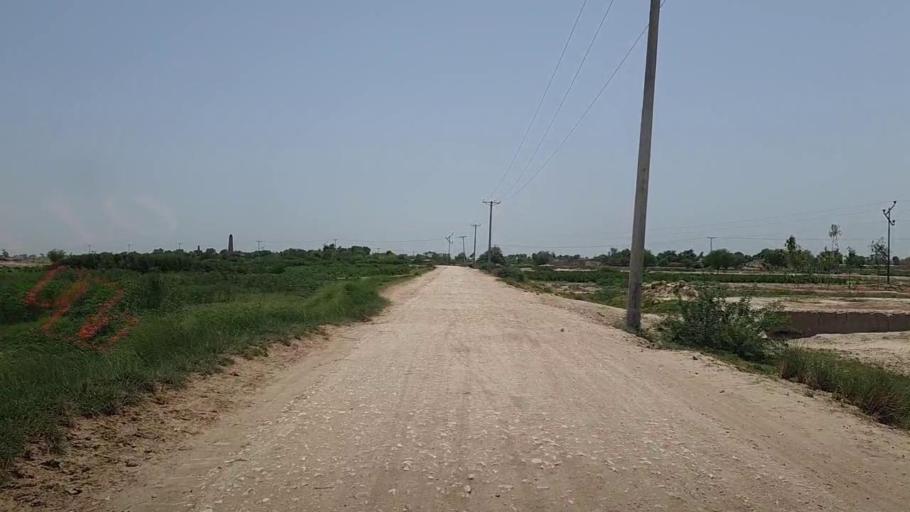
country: PK
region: Sindh
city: Pad Idan
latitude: 26.7730
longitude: 68.2921
